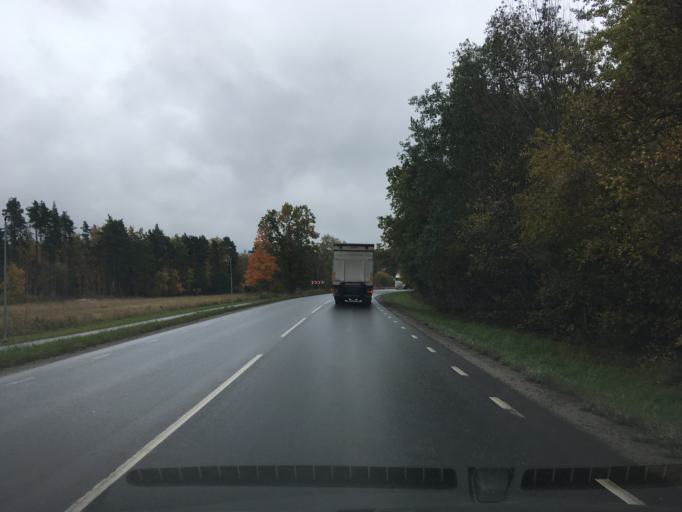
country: EE
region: Harju
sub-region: Saue vald
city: Laagri
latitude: 59.3749
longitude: 24.5837
